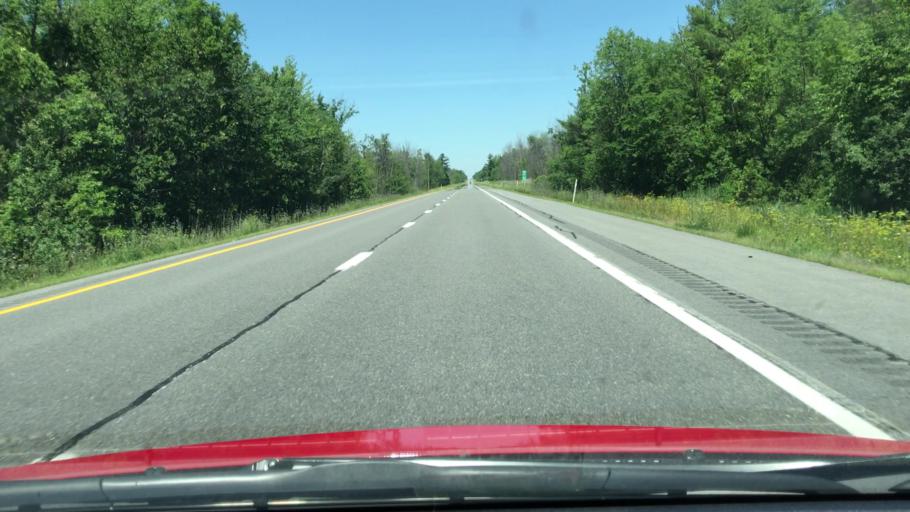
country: US
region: New York
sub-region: Clinton County
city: Champlain
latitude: 44.9365
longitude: -73.4468
